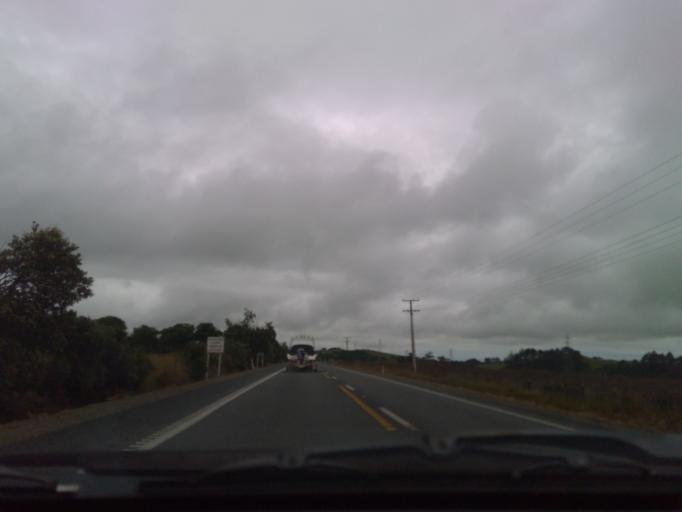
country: NZ
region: Northland
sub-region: Whangarei
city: Ruakaka
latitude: -36.0229
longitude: 174.4178
